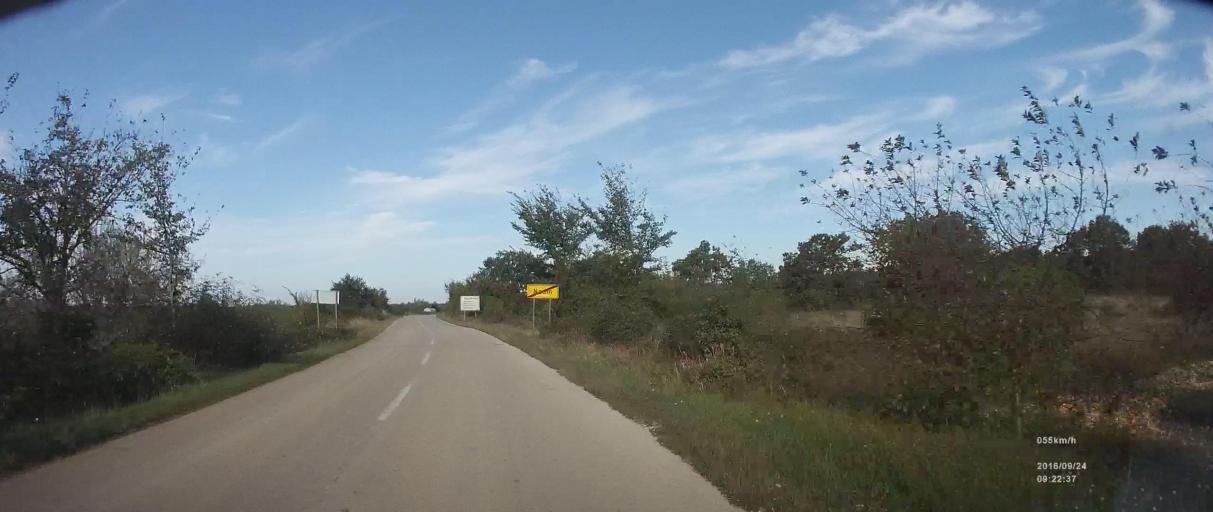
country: HR
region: Zadarska
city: Polaca
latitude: 44.0701
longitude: 15.4787
